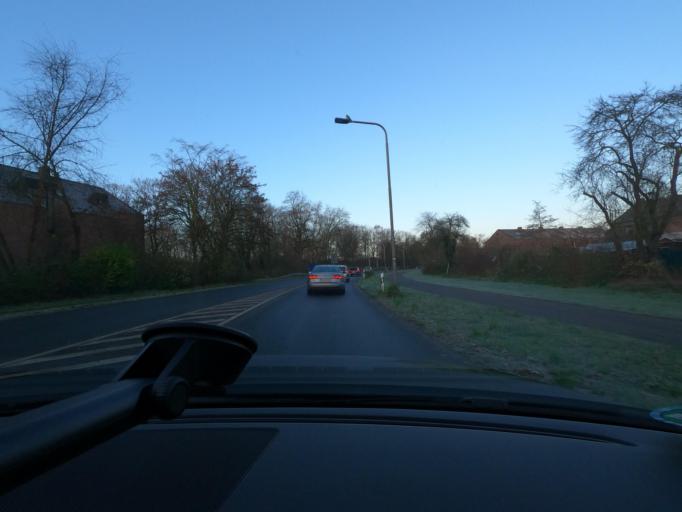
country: DE
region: North Rhine-Westphalia
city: Kempen
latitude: 51.3690
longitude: 6.4099
